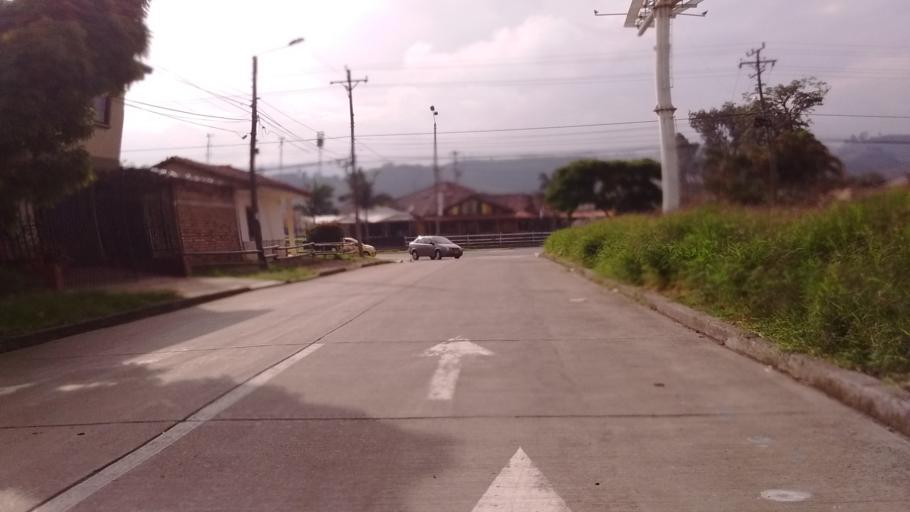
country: CO
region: Cauca
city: Popayan
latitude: 2.4549
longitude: -76.5934
